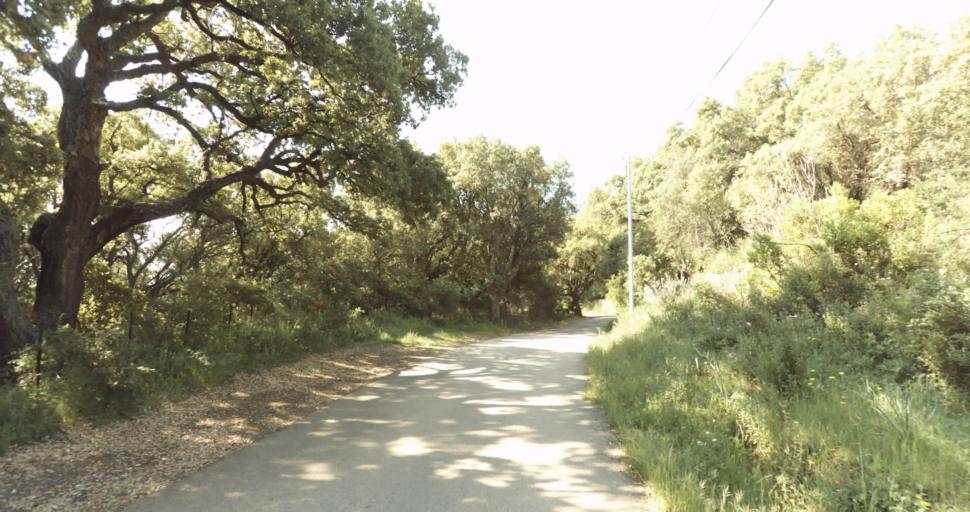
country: FR
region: Corsica
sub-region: Departement de la Haute-Corse
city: Furiani
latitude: 42.6390
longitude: 9.4163
